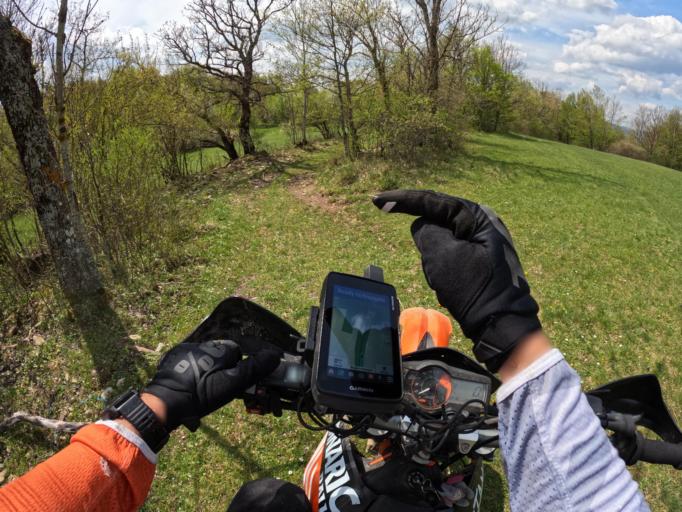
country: BA
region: Federation of Bosnia and Herzegovina
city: Bihac
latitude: 44.7184
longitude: 15.7712
